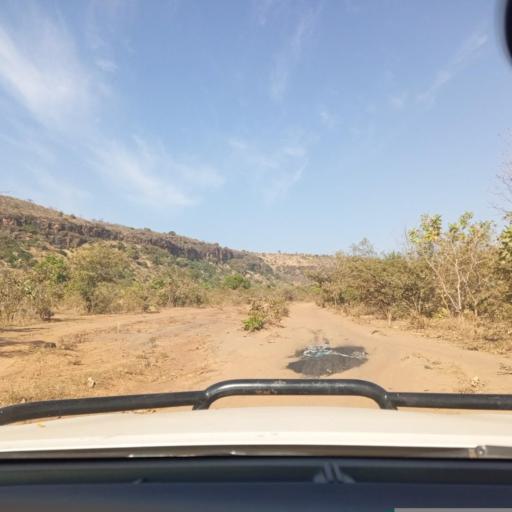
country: ML
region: Bamako
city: Bamako
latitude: 12.5572
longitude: -8.1495
